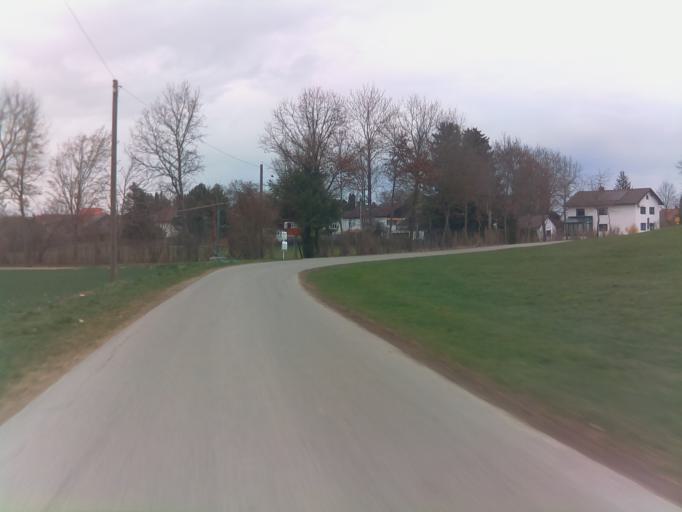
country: DE
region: Bavaria
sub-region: Upper Bavaria
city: Penzing
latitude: 48.0810
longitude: 10.9638
